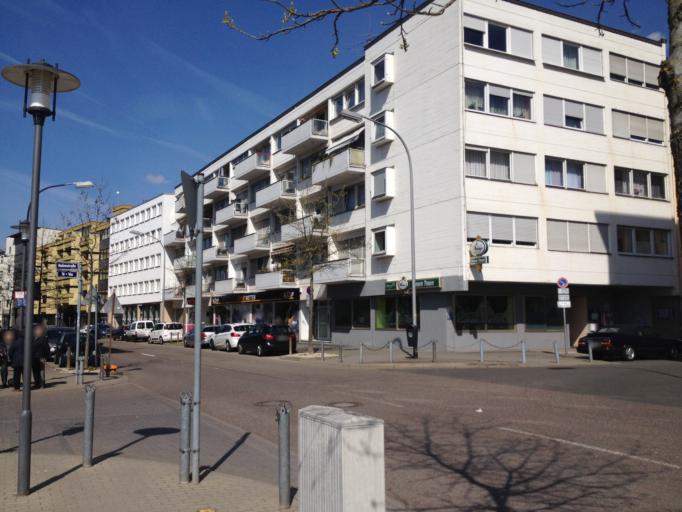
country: DE
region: Saarland
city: Saarbrucken
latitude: 49.2389
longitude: 6.9869
